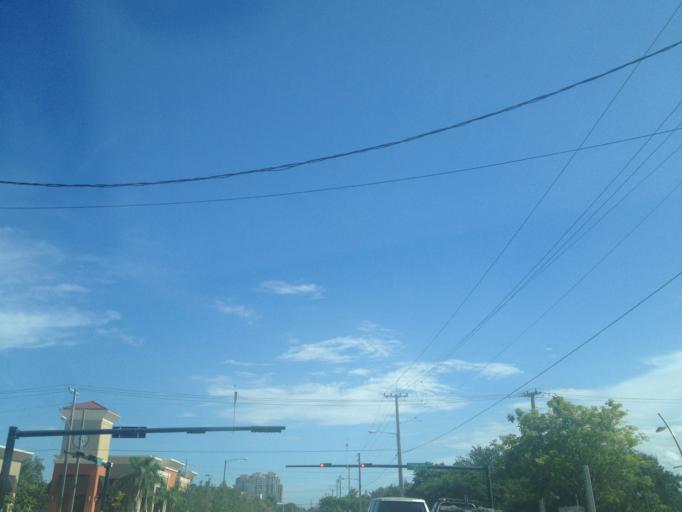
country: US
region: Florida
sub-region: Broward County
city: Fort Lauderdale
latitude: 26.1300
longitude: -80.1508
